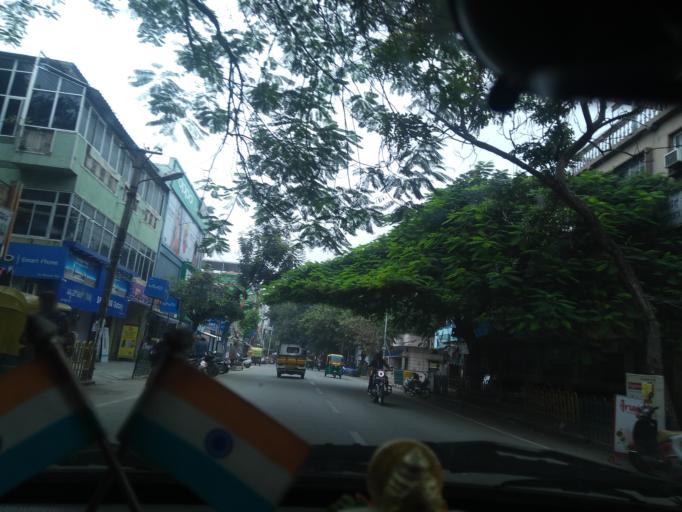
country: IN
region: Karnataka
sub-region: Bangalore Urban
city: Bangalore
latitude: 12.9984
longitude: 77.5509
